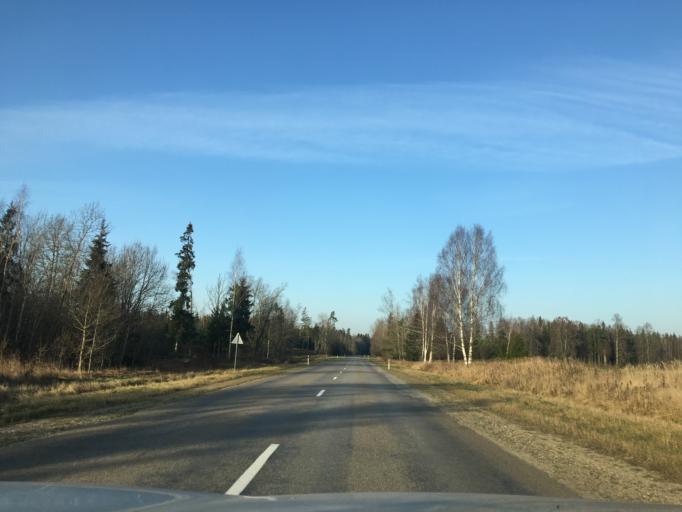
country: LV
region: Kuldigas Rajons
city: Kuldiga
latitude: 57.0413
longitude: 21.8304
